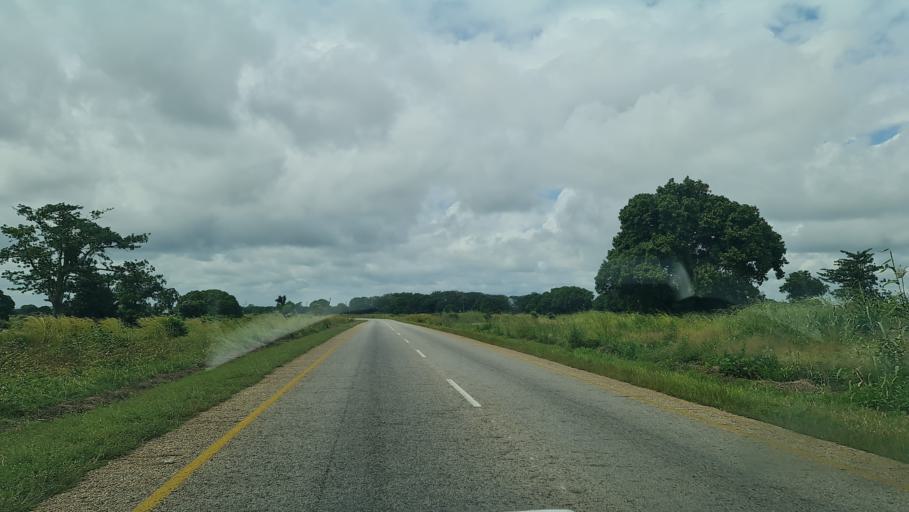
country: MZ
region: Nampula
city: Nampula
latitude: -14.9622
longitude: 39.8716
